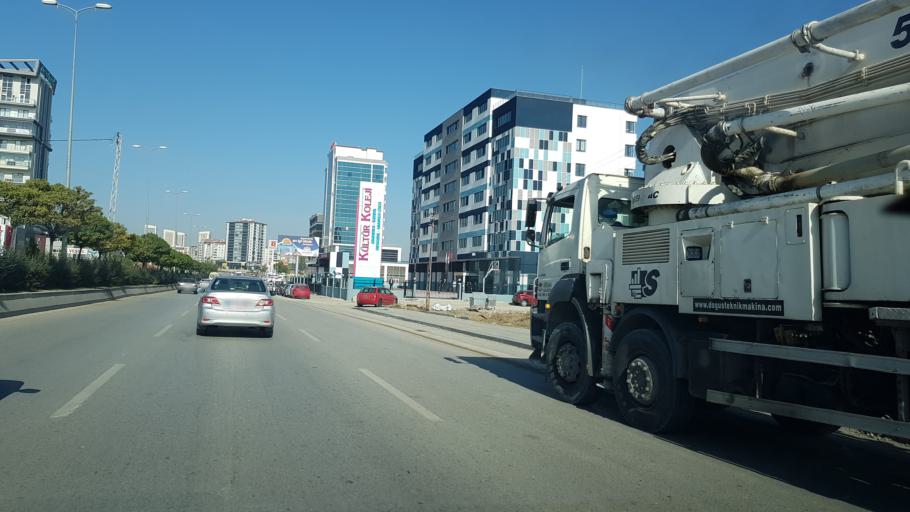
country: TR
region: Ankara
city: Etimesgut
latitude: 39.9651
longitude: 32.6071
